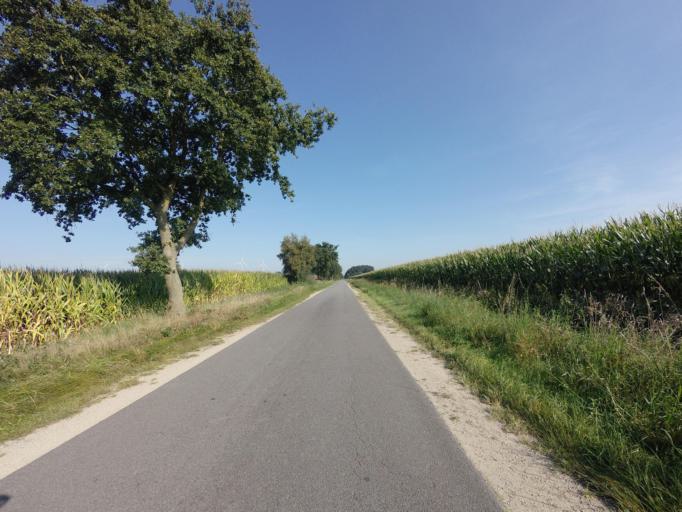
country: DE
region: Lower Saxony
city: Wielen
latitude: 52.5661
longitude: 6.7808
